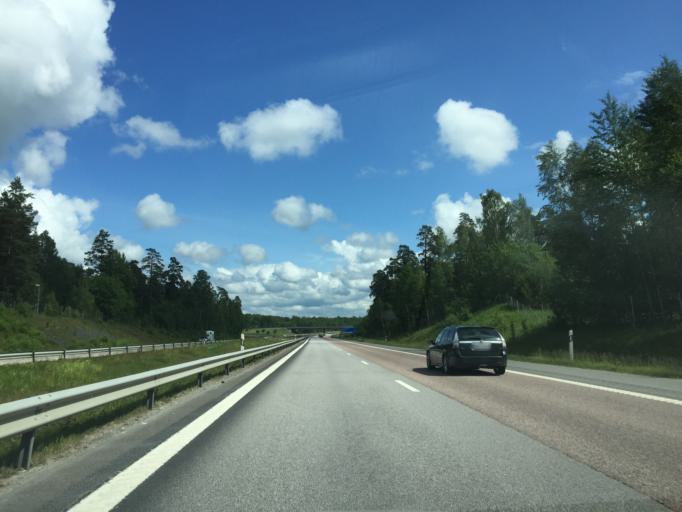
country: SE
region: OErebro
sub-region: Orebro Kommun
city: Orebro
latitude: 59.2999
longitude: 15.2505
